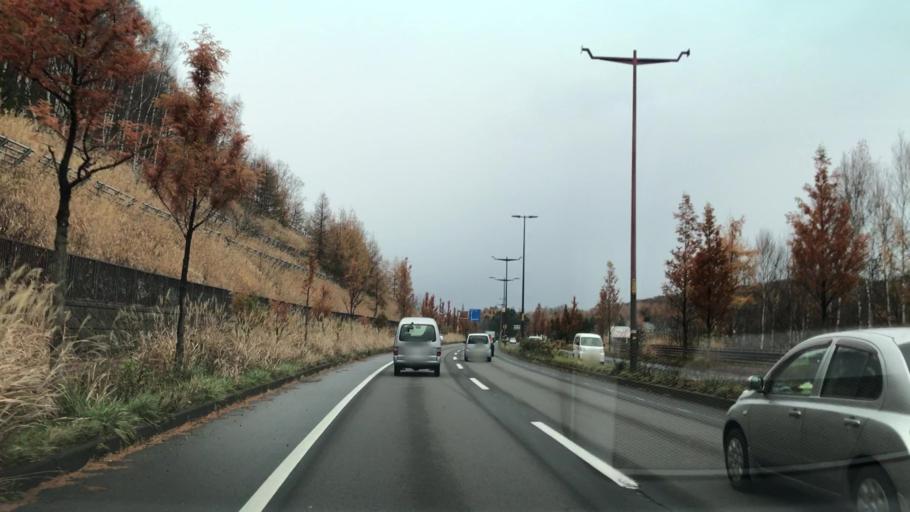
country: JP
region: Hokkaido
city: Otaru
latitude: 43.2146
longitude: 140.9578
